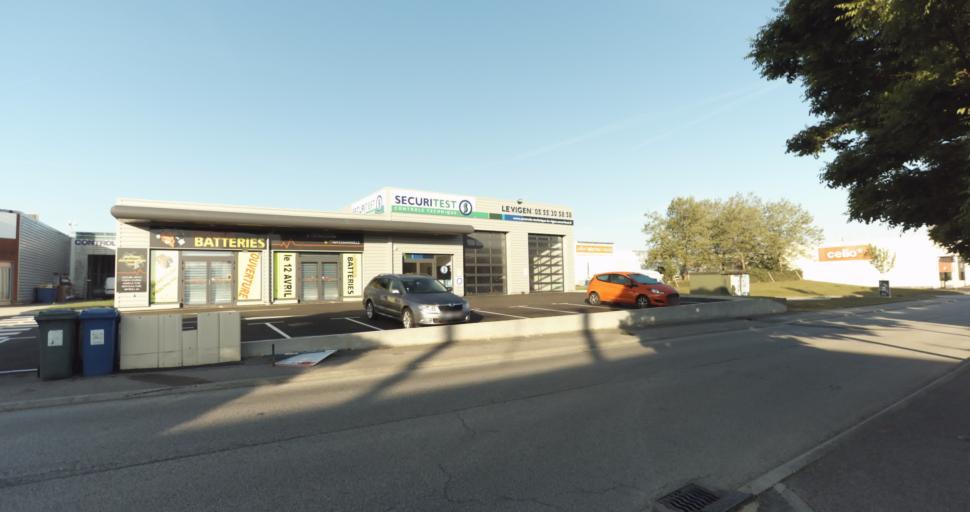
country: FR
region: Limousin
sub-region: Departement de la Haute-Vienne
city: Condat-sur-Vienne
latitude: 45.7807
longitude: 1.3084
